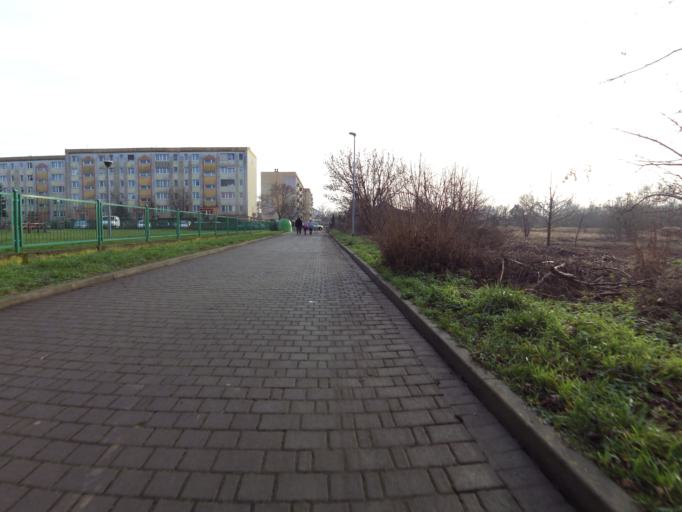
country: PL
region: West Pomeranian Voivodeship
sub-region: Powiat mysliborski
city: Debno
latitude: 52.7336
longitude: 14.6992
